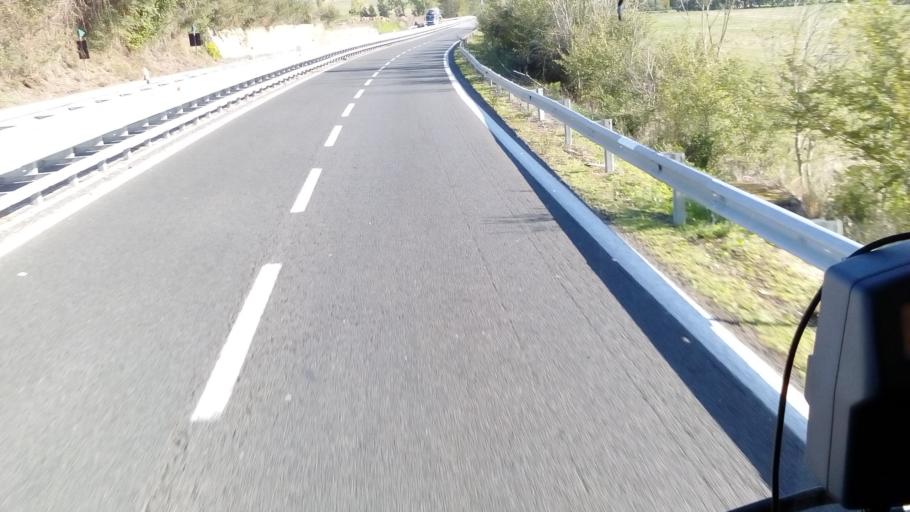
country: IT
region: Latium
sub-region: Provincia di Viterbo
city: Montalto di Castro
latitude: 42.3201
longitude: 11.6489
